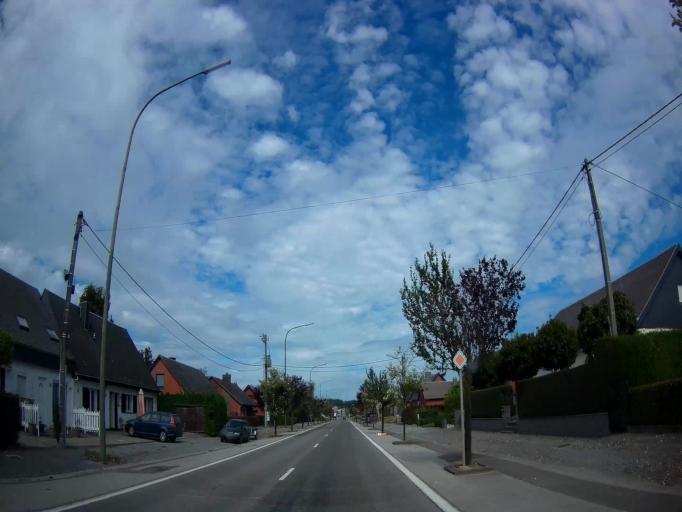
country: BE
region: Wallonia
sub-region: Province du Luxembourg
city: Hotton
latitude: 50.2735
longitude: 5.4514
